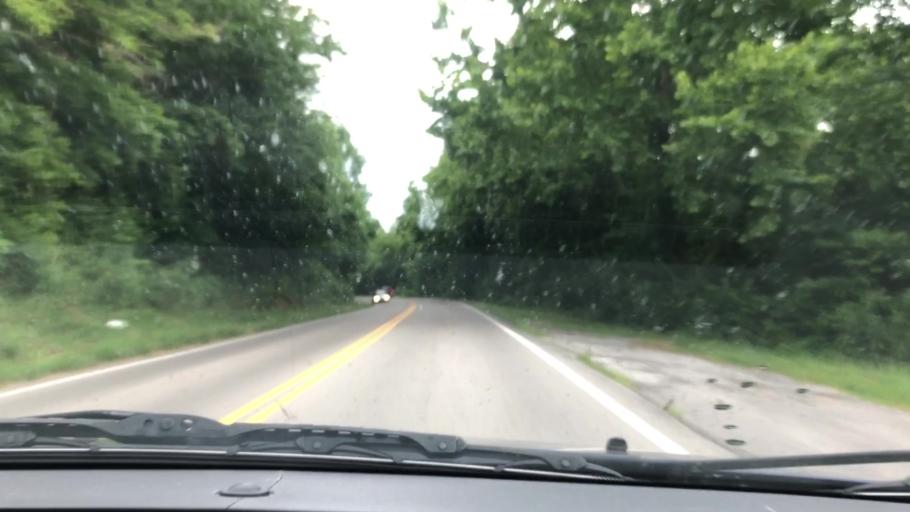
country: US
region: Tennessee
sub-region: Maury County
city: Columbia
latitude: 35.6911
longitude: -87.0099
